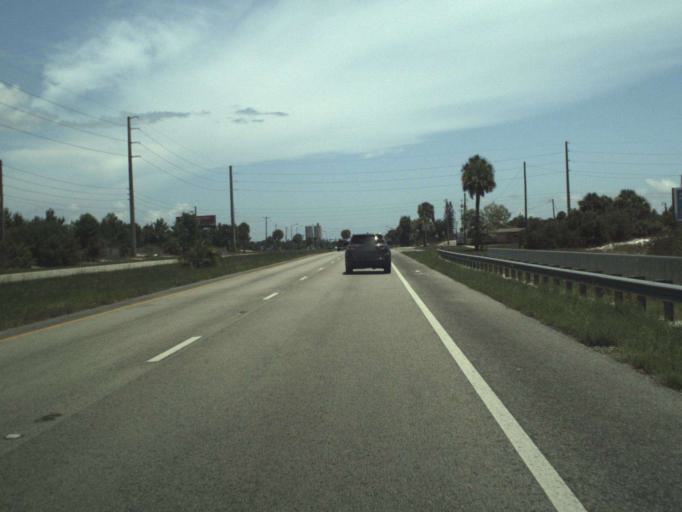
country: US
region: Florida
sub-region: Saint Lucie County
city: Fort Pierce North
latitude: 27.4751
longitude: -80.3369
